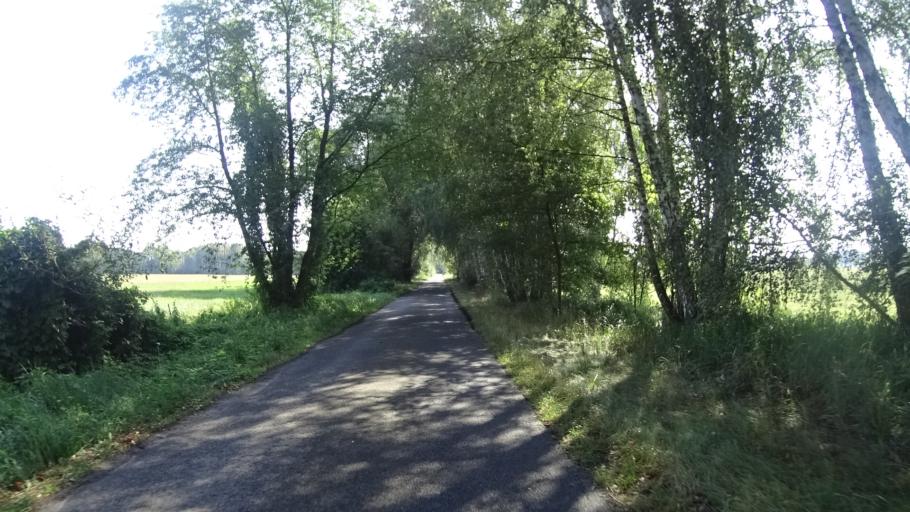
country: DE
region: Brandenburg
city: Straupitz
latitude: 51.8952
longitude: 14.1192
